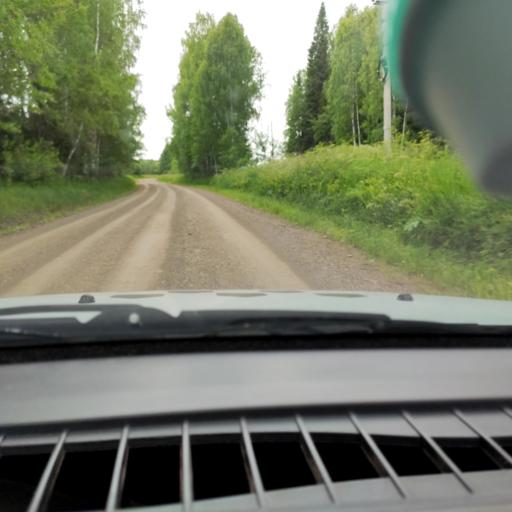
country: RU
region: Perm
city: Suksun
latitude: 57.2050
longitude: 57.6261
